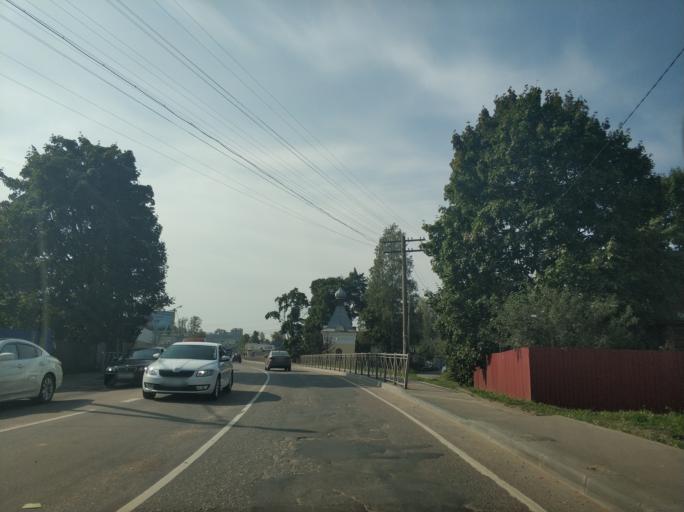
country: RU
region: Leningrad
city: Murino
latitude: 60.0452
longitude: 30.4485
